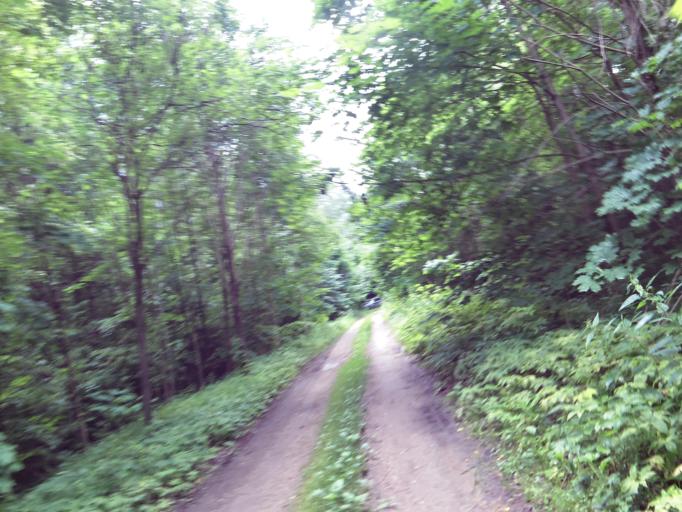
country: RU
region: Moskovskaya
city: Popovo
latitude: 54.9556
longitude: 37.7040
